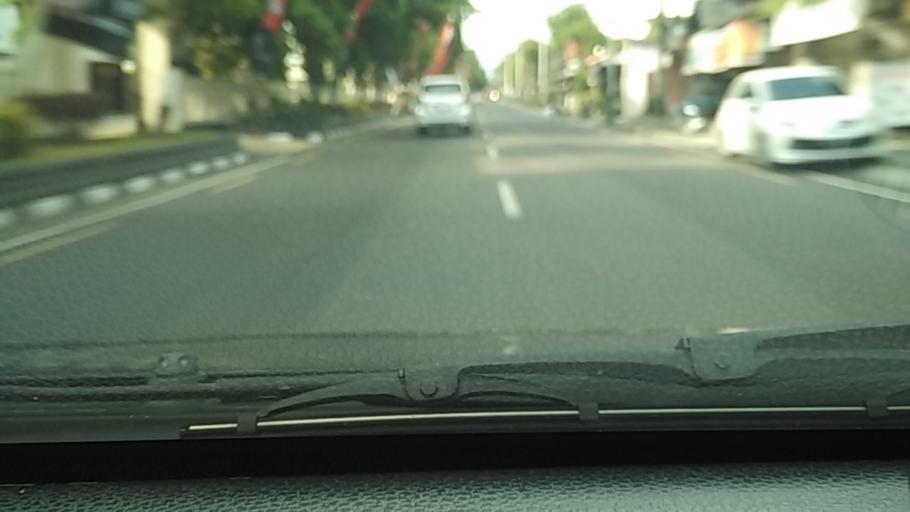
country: ID
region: Daerah Istimewa Yogyakarta
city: Yogyakarta
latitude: -7.8001
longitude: 110.3845
